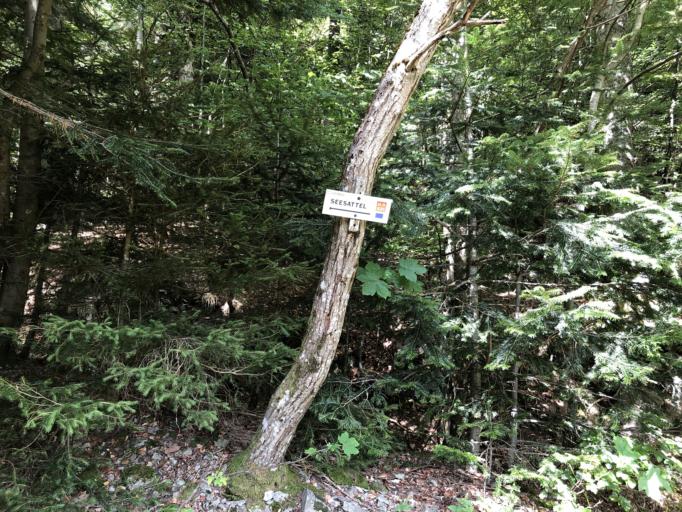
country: FR
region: Alsace
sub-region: Departement du Haut-Rhin
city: Kruth
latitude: 47.9996
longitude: 6.9492
